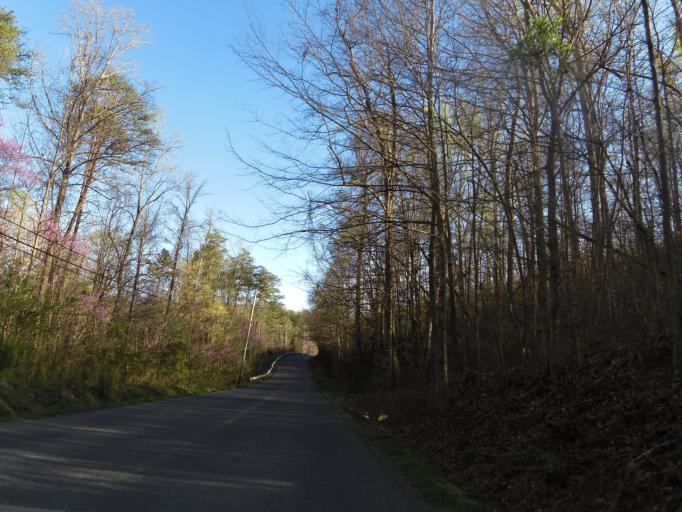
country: US
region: Tennessee
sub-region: Knox County
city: Mascot
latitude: 35.9995
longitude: -83.7656
